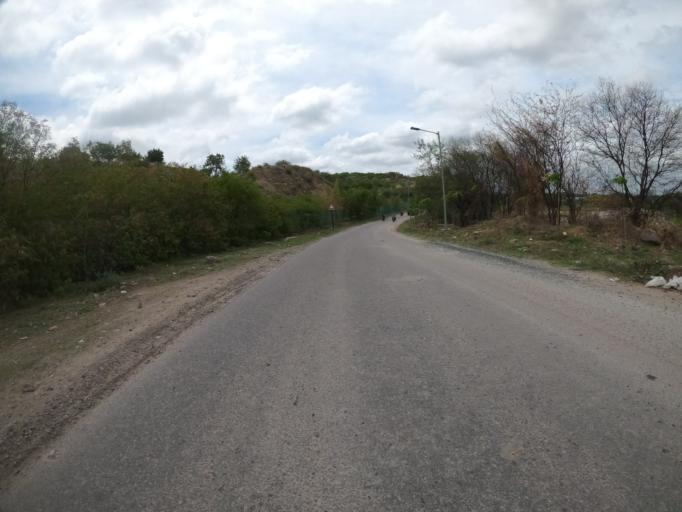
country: IN
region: Telangana
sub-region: Hyderabad
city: Hyderabad
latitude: 17.3120
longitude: 78.3747
